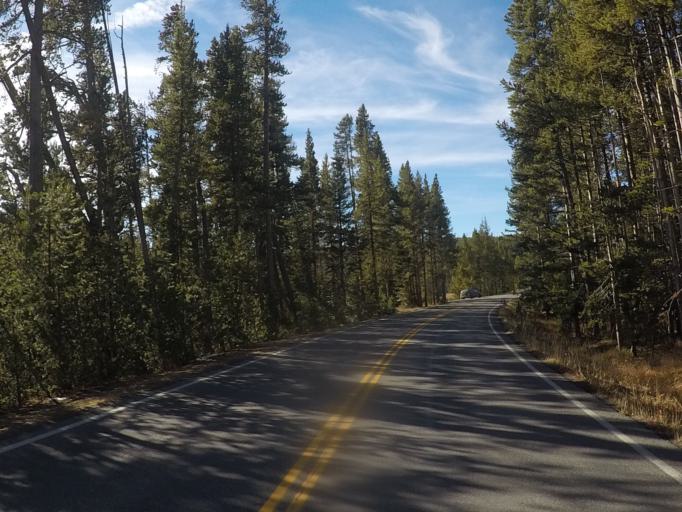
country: US
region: Montana
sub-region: Gallatin County
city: West Yellowstone
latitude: 44.7049
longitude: -110.5036
